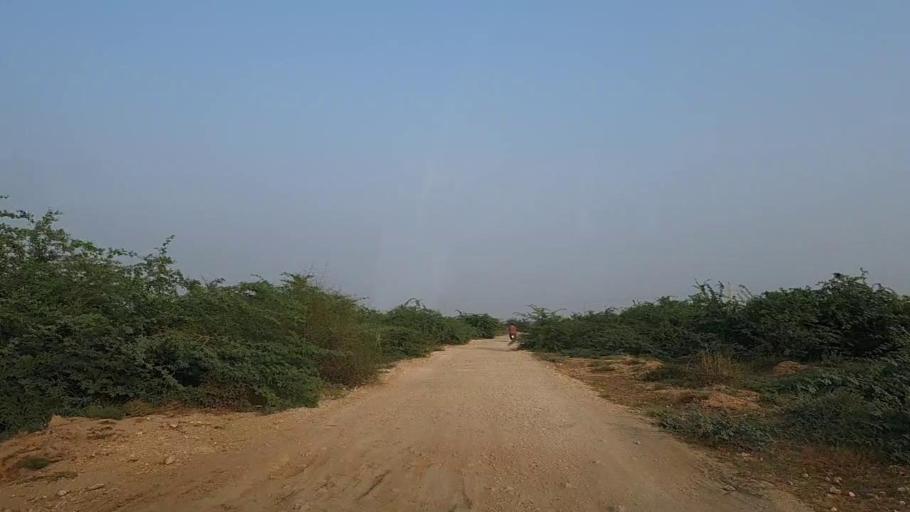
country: PK
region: Sindh
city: Thatta
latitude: 24.6909
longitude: 67.8445
